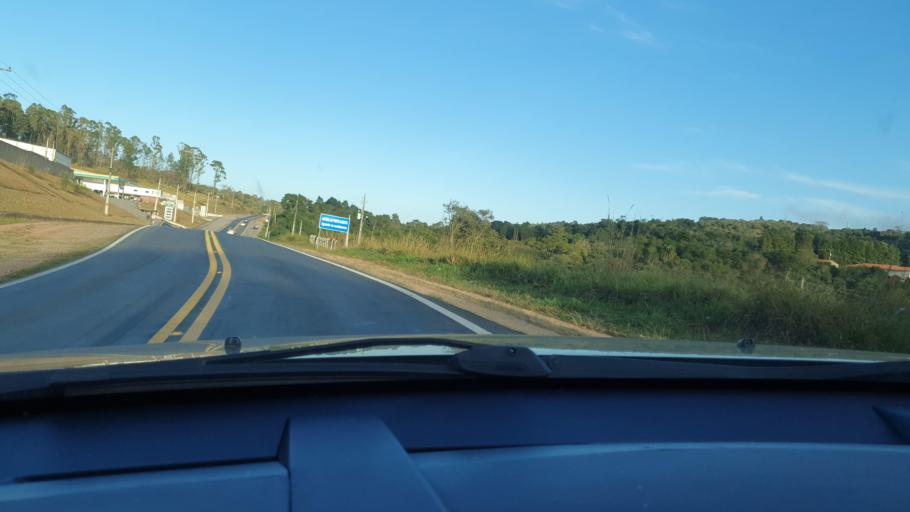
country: BR
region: Sao Paulo
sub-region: Ibiuna
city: Ibiuna
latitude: -23.6744
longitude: -47.3157
